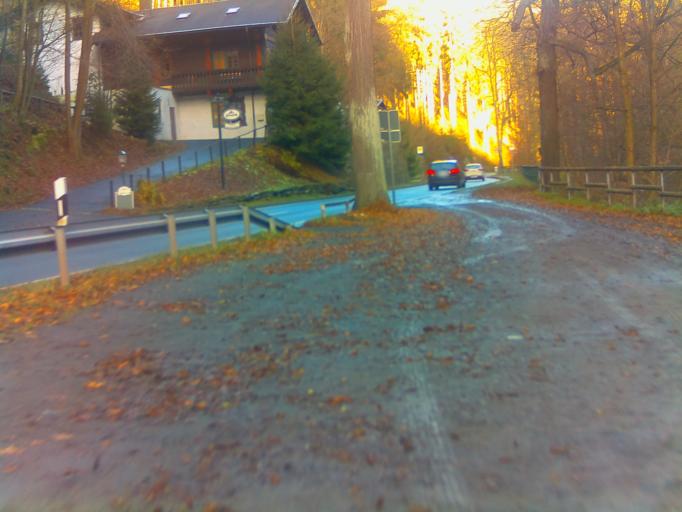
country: DE
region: Thuringia
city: Schwarzburg
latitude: 50.6588
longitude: 11.2154
